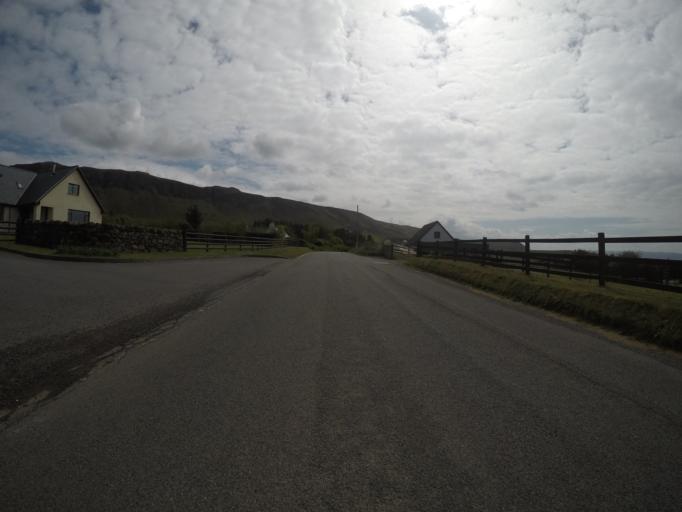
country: GB
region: Scotland
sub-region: Highland
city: Portree
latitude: 57.6189
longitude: -6.3724
